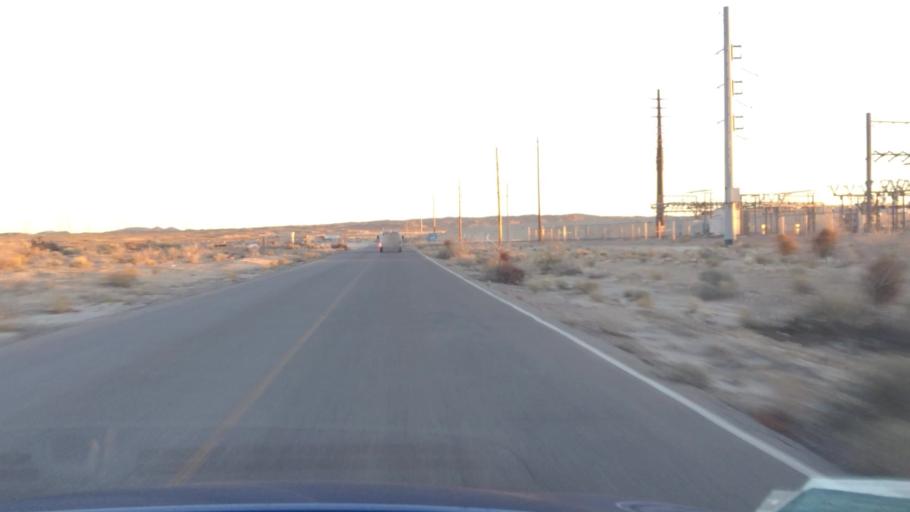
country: US
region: Nevada
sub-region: Clark County
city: Nellis Air Force Base
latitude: 36.2203
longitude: -114.8907
